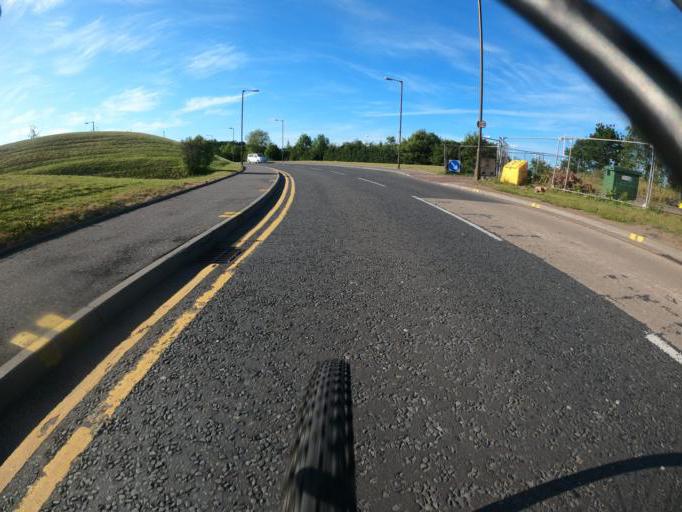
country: GB
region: Scotland
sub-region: West Lothian
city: Seafield
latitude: 55.9222
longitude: -3.1321
